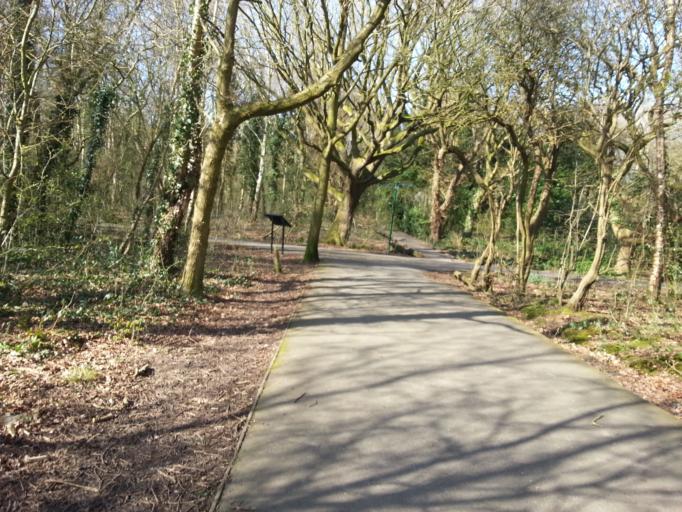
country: GB
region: England
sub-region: Knowsley
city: Huyton
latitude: 53.3661
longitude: -2.8412
